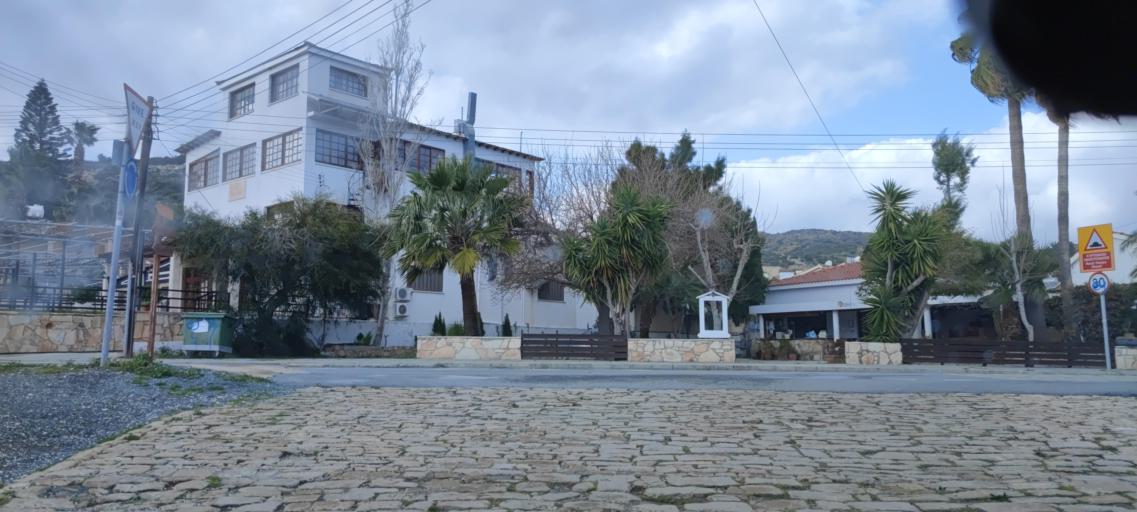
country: CY
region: Limassol
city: Pissouri
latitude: 34.6509
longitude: 32.7236
